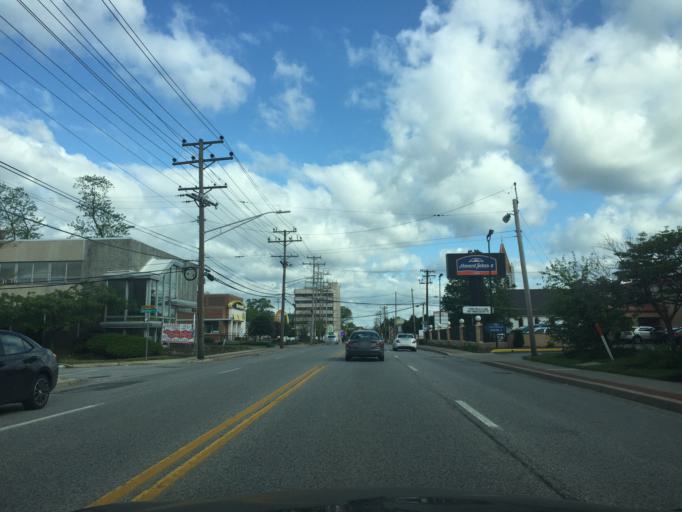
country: US
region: Maryland
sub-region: Baltimore County
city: Pikesville
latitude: 39.3669
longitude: -76.7157
